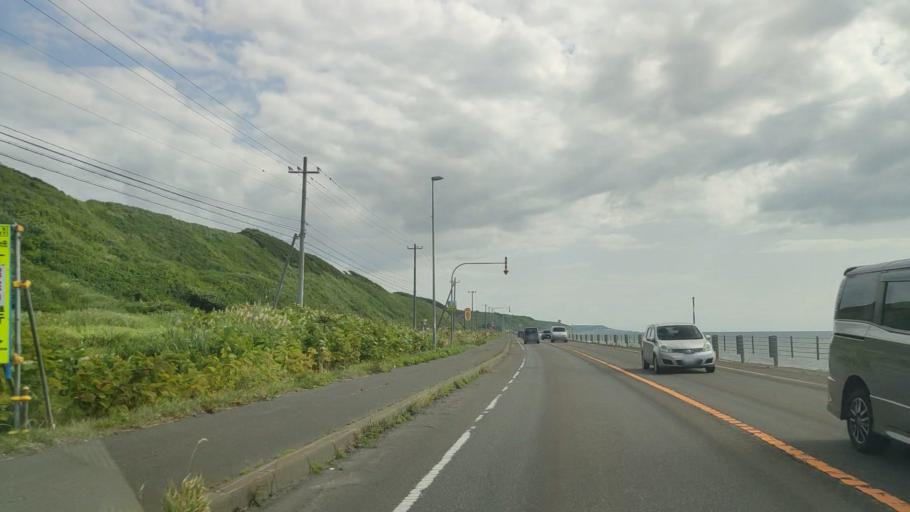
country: JP
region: Hokkaido
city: Rumoi
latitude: 44.2125
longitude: 141.6563
